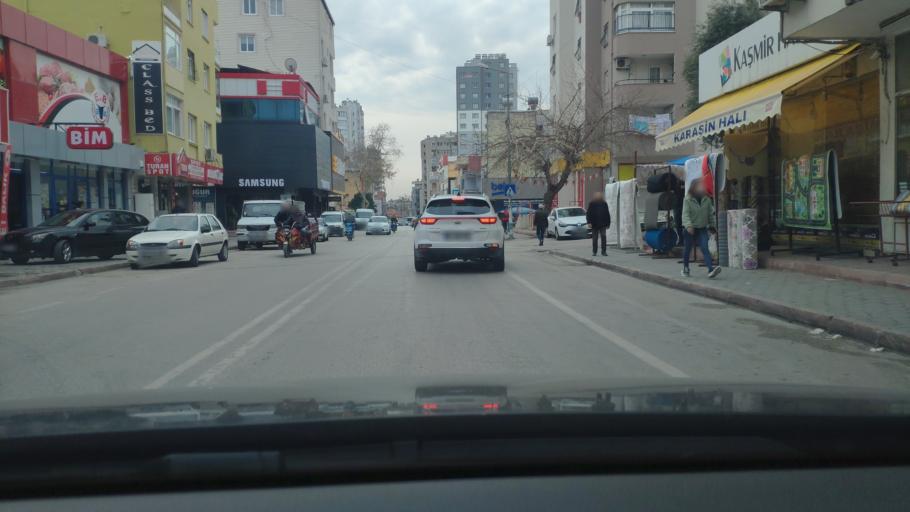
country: TR
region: Adana
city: Adana
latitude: 37.0245
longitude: 35.3126
